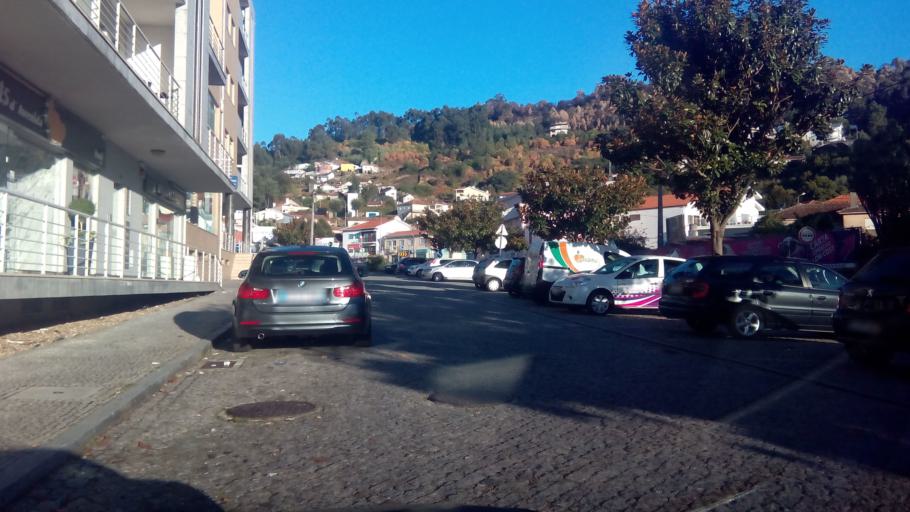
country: PT
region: Porto
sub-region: Paredes
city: Baltar
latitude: 41.1922
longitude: -8.3873
